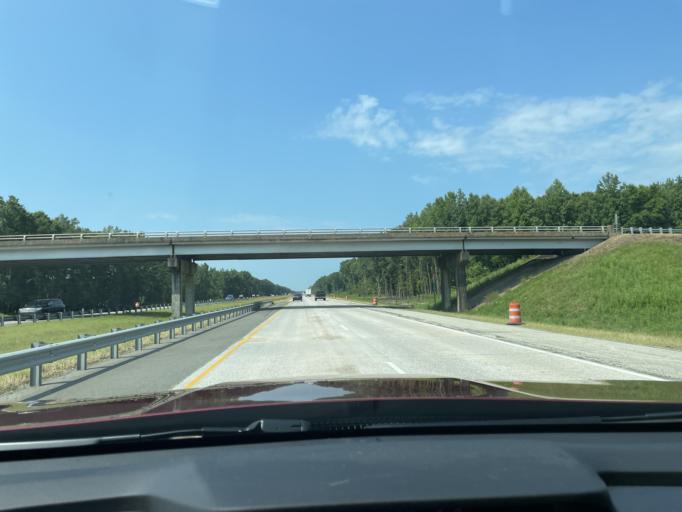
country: US
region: Arkansas
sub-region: White County
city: Searcy
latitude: 35.1720
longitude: -91.7686
